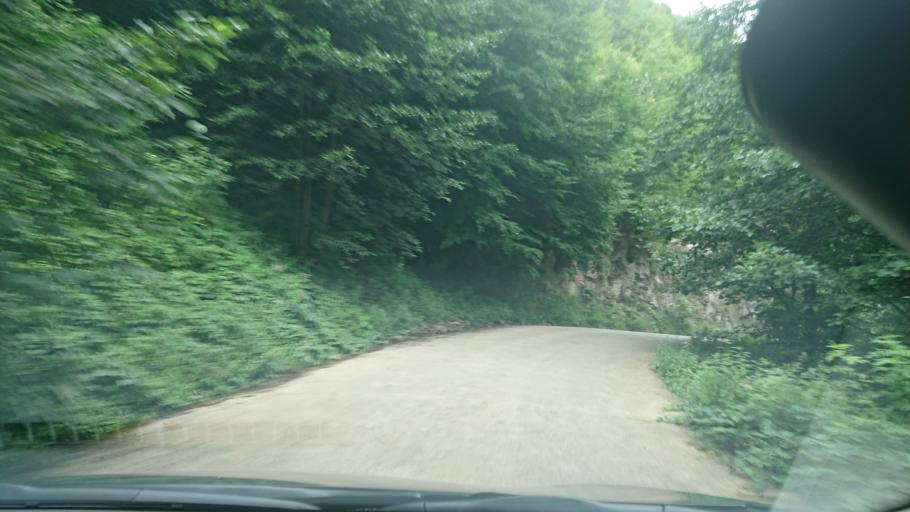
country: TR
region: Gumushane
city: Kurtun
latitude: 40.6763
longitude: 39.0425
